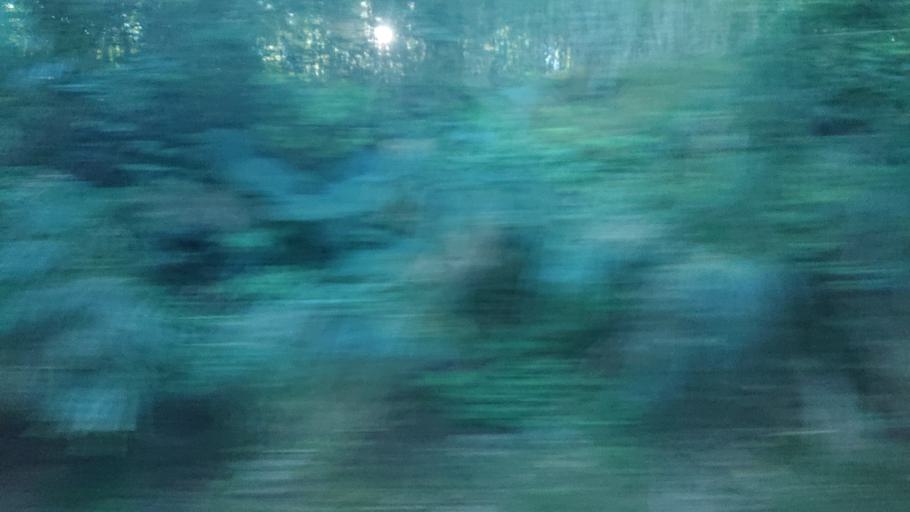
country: TW
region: Taiwan
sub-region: Chiayi
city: Jiayi Shi
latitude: 23.5310
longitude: 120.6303
